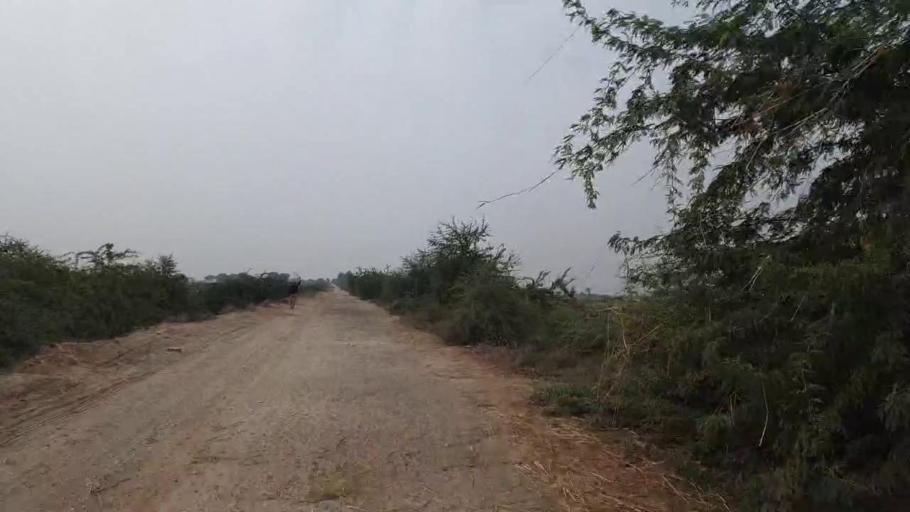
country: PK
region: Sindh
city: Kario
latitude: 24.9030
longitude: 68.5311
